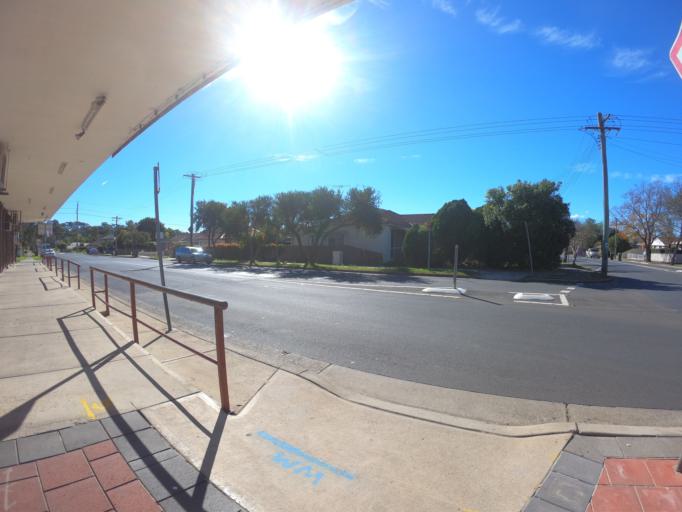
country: AU
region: New South Wales
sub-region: Hawkesbury
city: South Windsor
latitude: -33.6167
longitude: 150.8082
